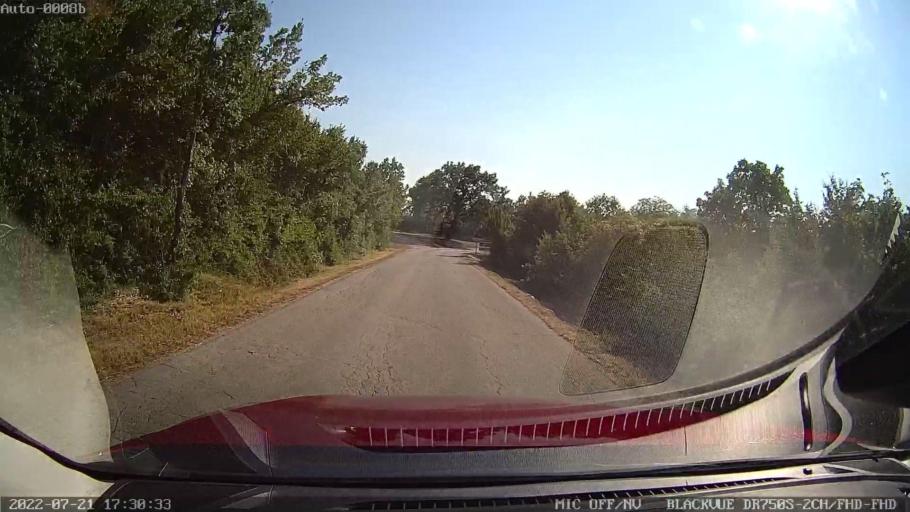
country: HR
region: Istarska
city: Karojba
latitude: 45.1757
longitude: 13.7734
